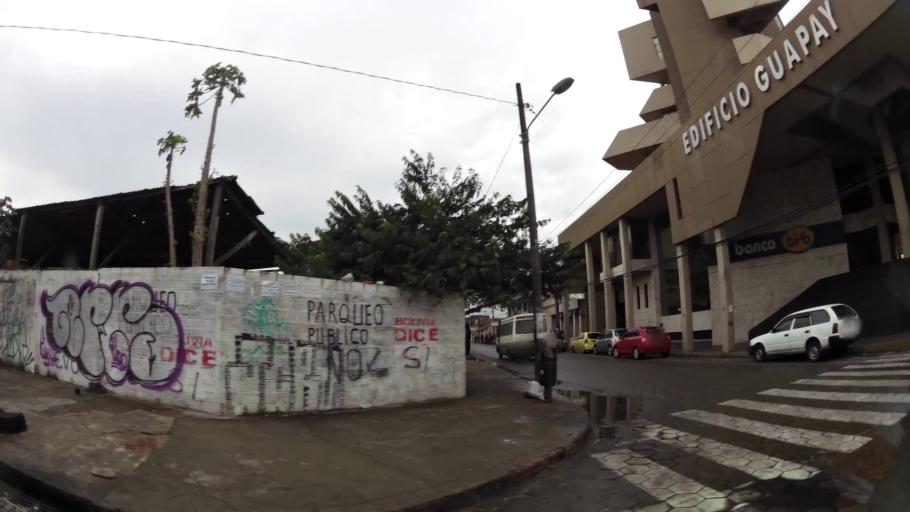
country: BO
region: Santa Cruz
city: Santa Cruz de la Sierra
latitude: -17.7832
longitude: -63.1772
